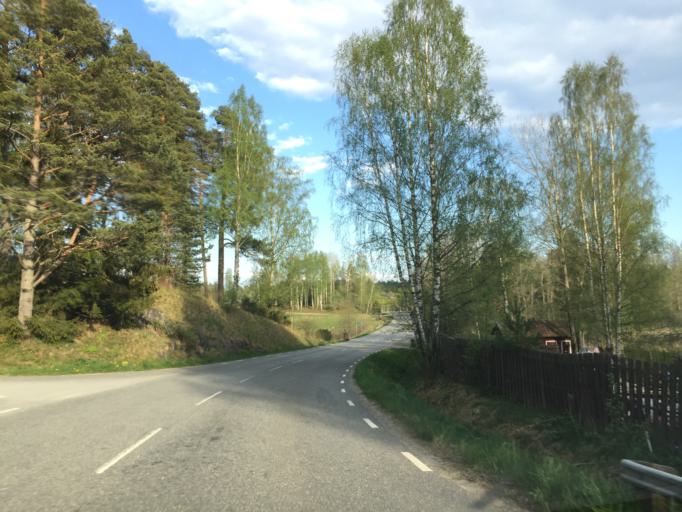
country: SE
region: OErebro
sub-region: Orebro Kommun
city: Hovsta
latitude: 59.3856
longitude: 15.2049
